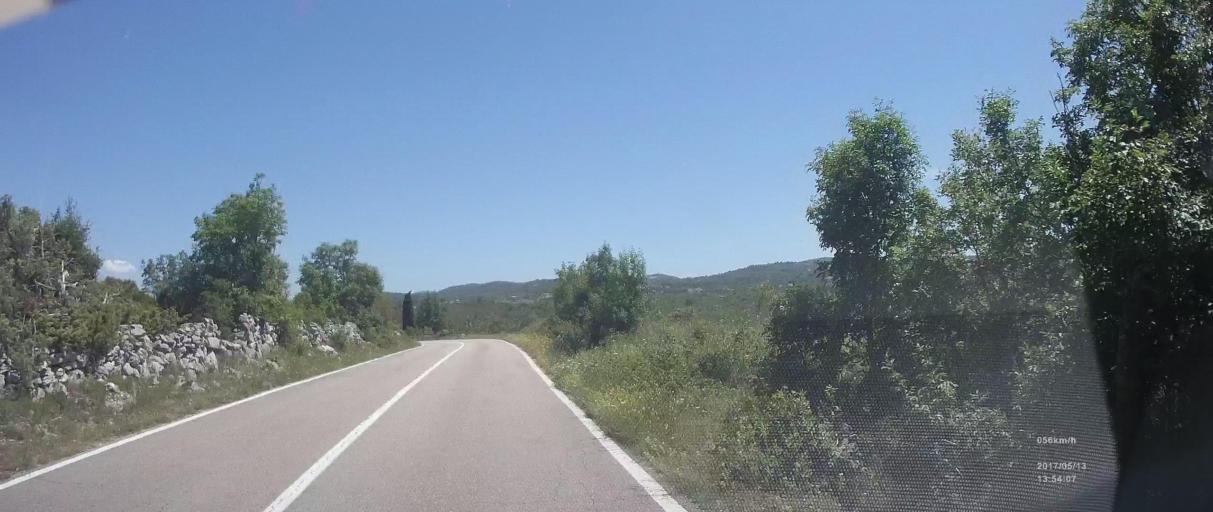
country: HR
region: Sibensko-Kniniska
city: Rogoznica
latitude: 43.5961
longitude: 16.0041
